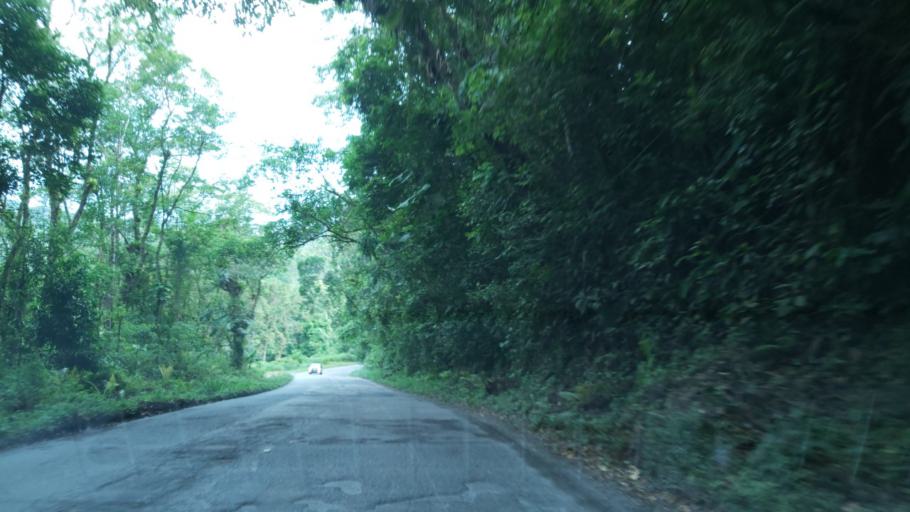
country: BR
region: Sao Paulo
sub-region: Juquia
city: Juquia
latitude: -24.0695
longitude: -47.6026
